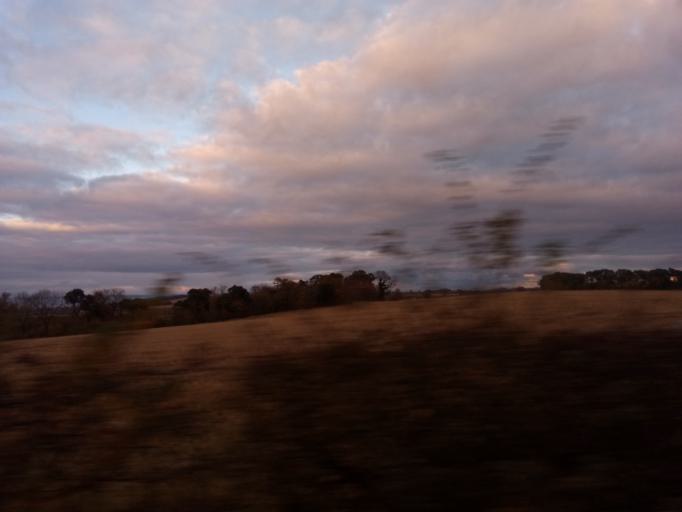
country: GB
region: Scotland
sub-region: Midlothian
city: Gorebridge
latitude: 55.8830
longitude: -3.0225
